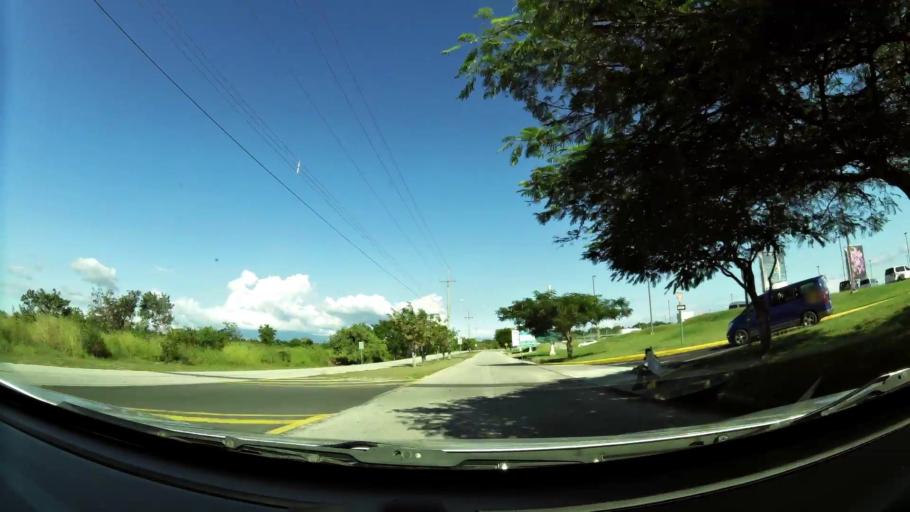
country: CR
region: Guanacaste
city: Liberia
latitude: 10.6019
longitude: -85.5349
